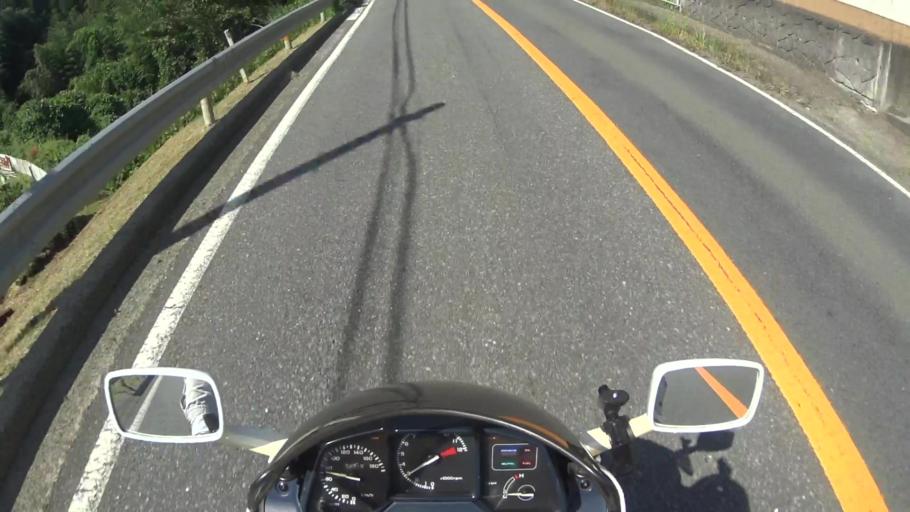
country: JP
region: Kyoto
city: Ayabe
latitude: 35.2982
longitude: 135.3234
